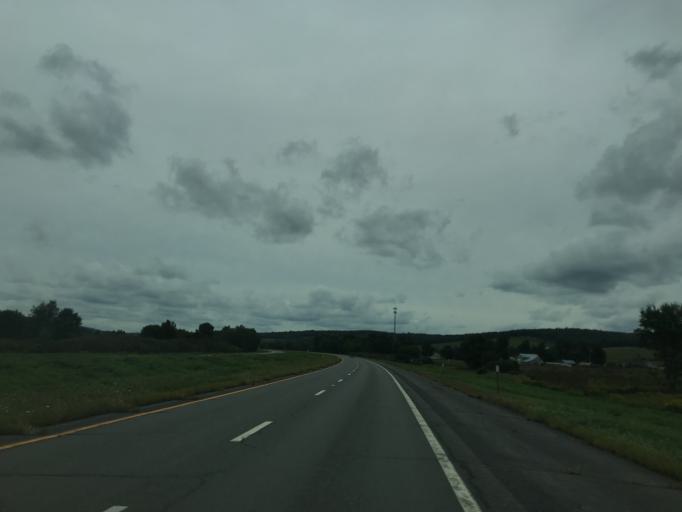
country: US
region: New York
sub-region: Chenango County
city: Bainbridge
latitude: 42.2622
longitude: -75.4681
